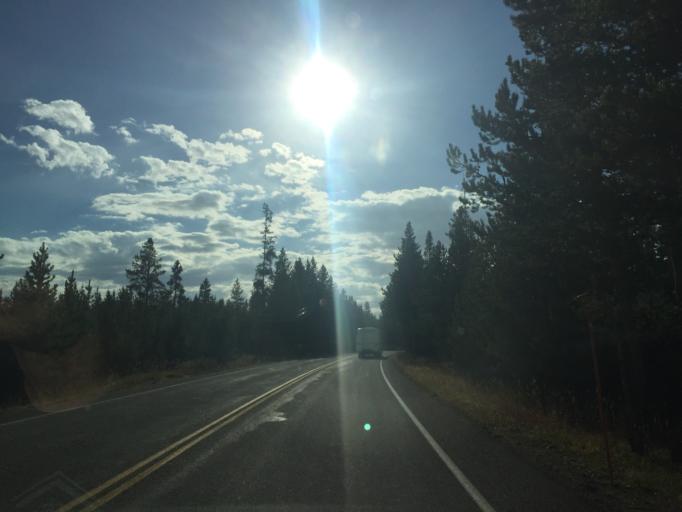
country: US
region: Montana
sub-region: Gallatin County
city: West Yellowstone
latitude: 44.6524
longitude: -110.9950
